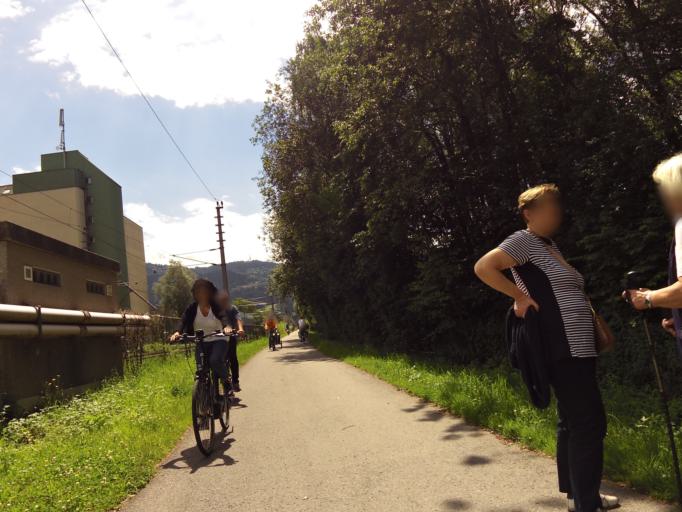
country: AT
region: Vorarlberg
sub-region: Politischer Bezirk Bregenz
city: Lochau
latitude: 47.5341
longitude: 9.7362
